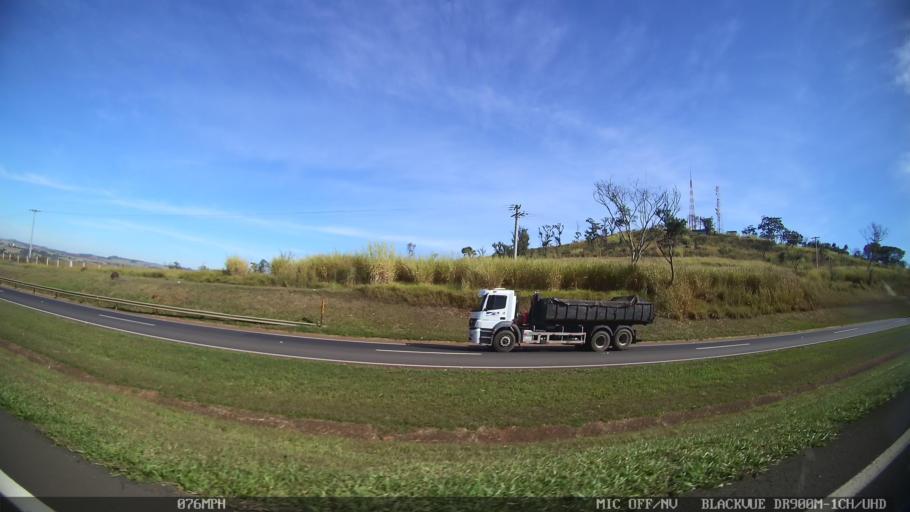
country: BR
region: Sao Paulo
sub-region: Leme
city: Leme
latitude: -22.1597
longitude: -47.3998
